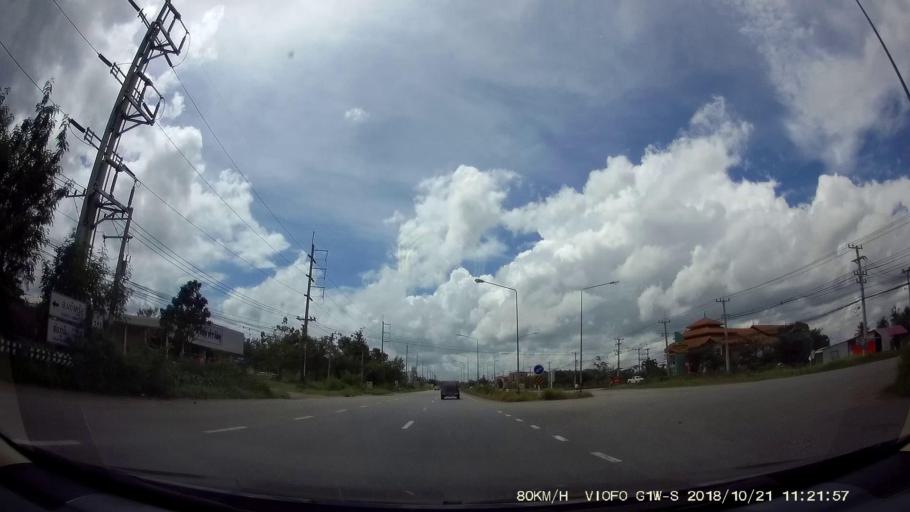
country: TH
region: Chaiyaphum
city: Chaiyaphum
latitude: 15.8410
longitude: 102.0620
